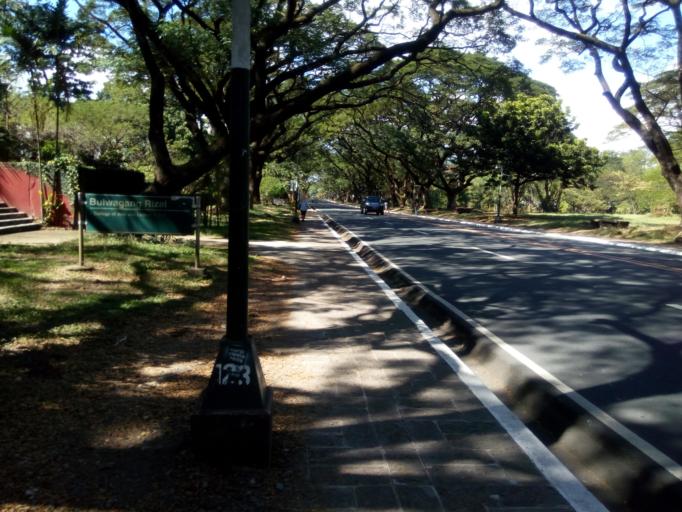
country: PH
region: Metro Manila
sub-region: Quezon City
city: Quezon City
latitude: 14.6538
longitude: 121.0681
